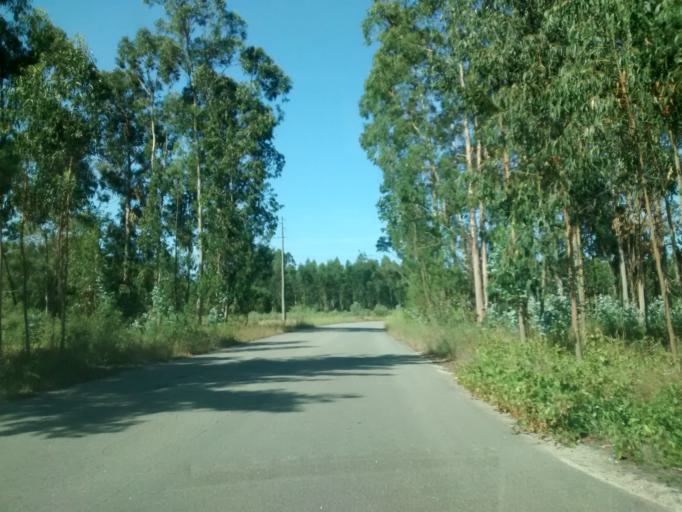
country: PT
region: Coimbra
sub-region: Cantanhede
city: Cantanhede
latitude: 40.4234
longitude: -8.6068
